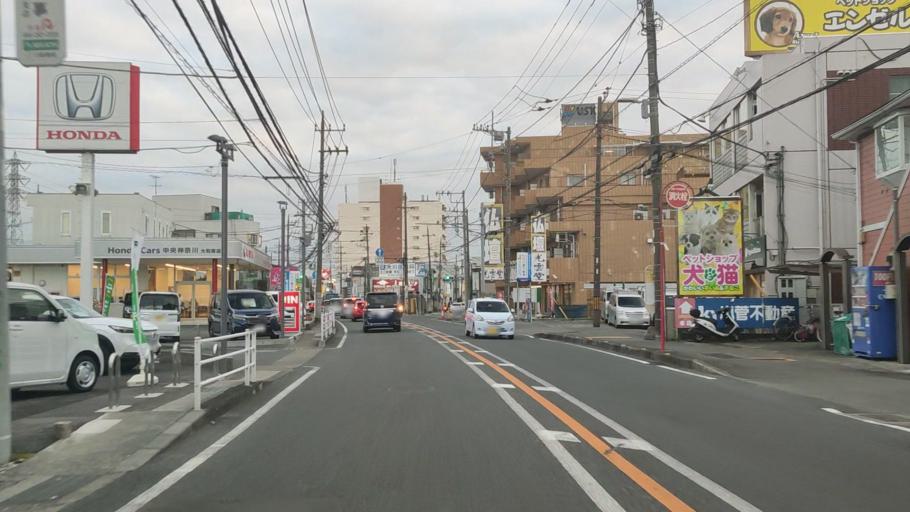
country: JP
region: Kanagawa
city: Minami-rinkan
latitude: 35.4537
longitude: 139.4668
